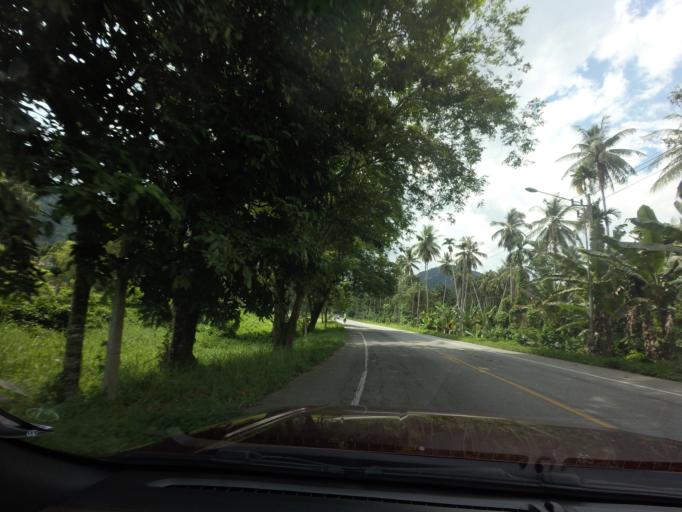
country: TH
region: Yala
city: Than To
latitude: 6.1947
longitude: 101.1737
